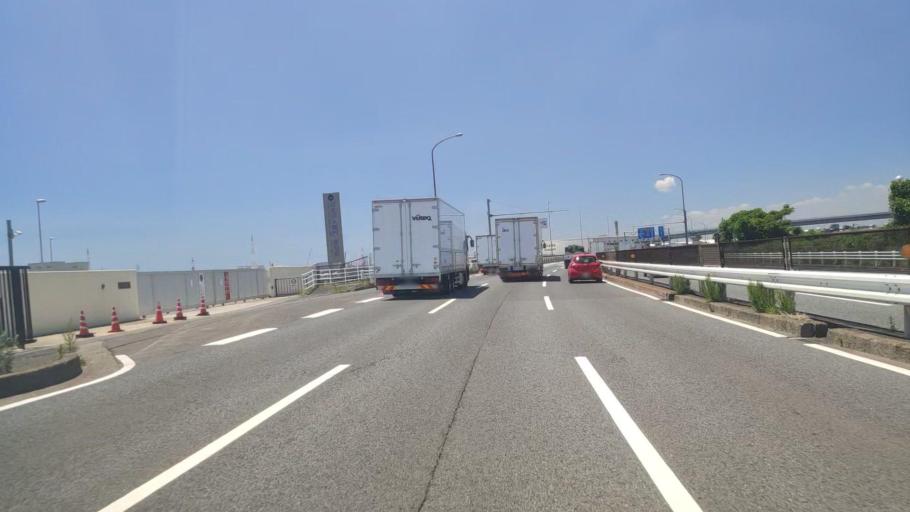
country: JP
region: Aichi
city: Kanie
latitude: 35.0787
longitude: 136.8229
